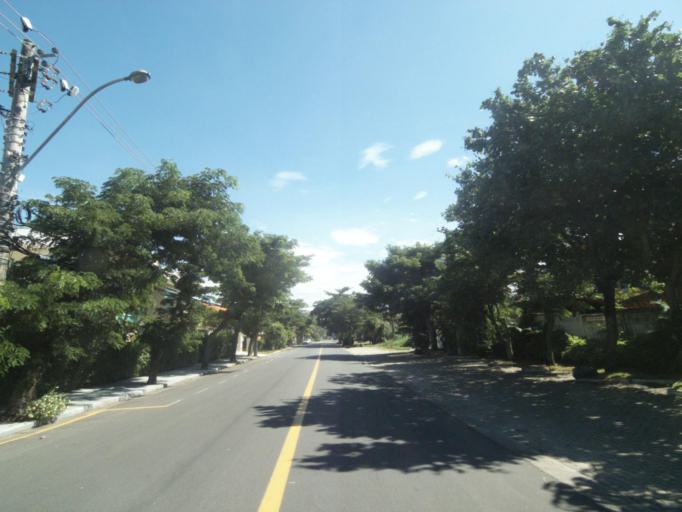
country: BR
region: Rio de Janeiro
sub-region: Niteroi
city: Niteroi
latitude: -22.9559
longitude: -43.0578
